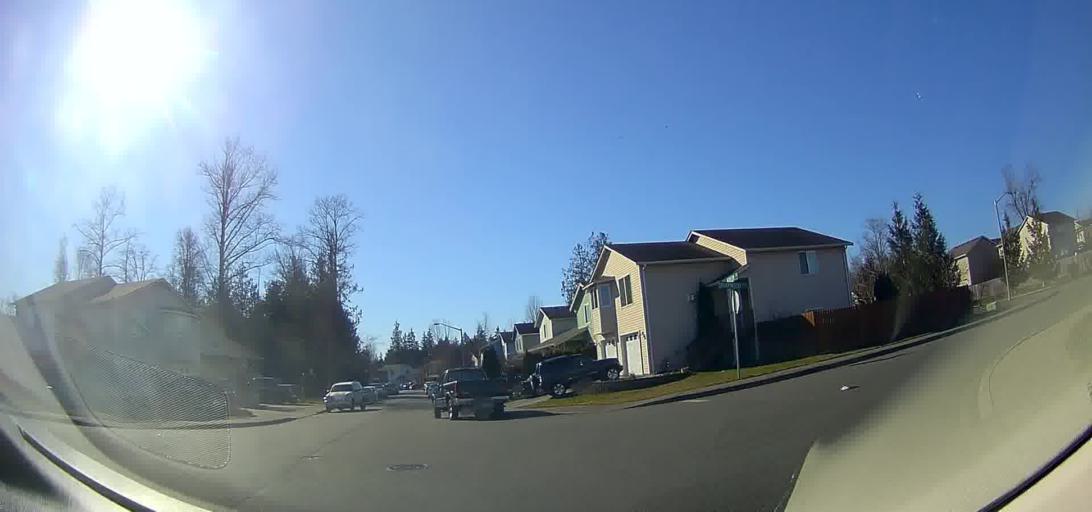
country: US
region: Washington
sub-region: Skagit County
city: Burlington
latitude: 48.4461
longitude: -122.2988
